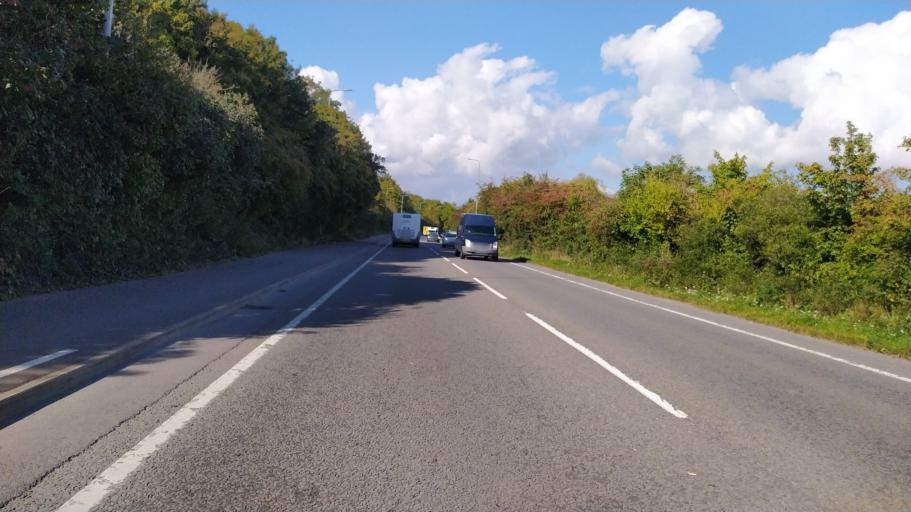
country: GB
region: England
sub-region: Dorset
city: Weymouth
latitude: 50.6251
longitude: -2.4714
